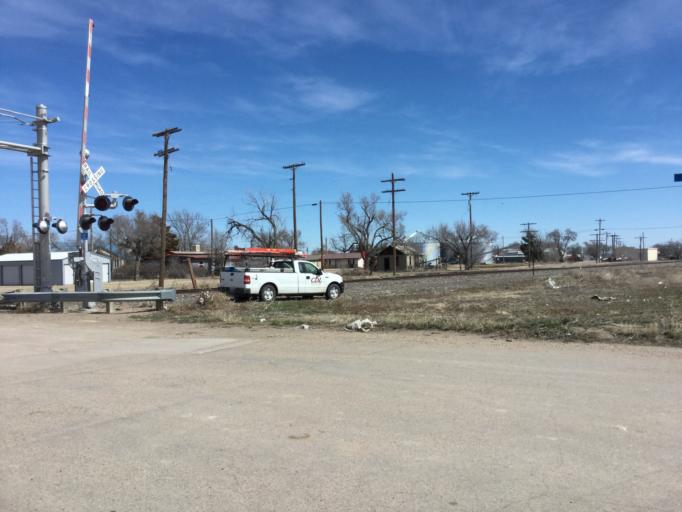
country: US
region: Kansas
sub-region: Greeley County
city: Tribune
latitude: 38.4676
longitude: -101.7565
